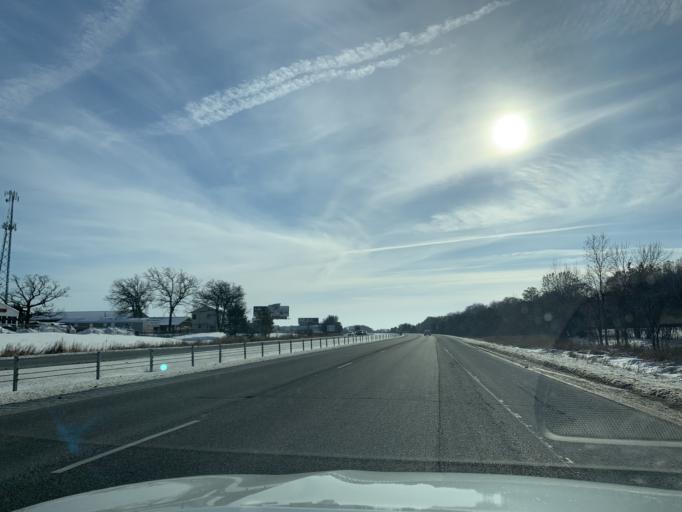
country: US
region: Minnesota
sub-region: Chisago County
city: Wyoming
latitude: 45.3325
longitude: -93.0049
